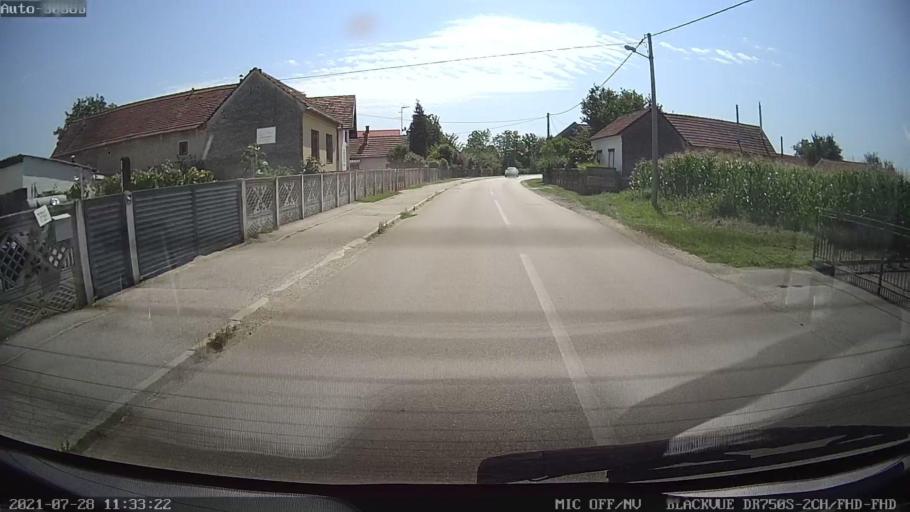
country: HR
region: Medimurska
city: Kursanec
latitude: 46.2853
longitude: 16.3857
